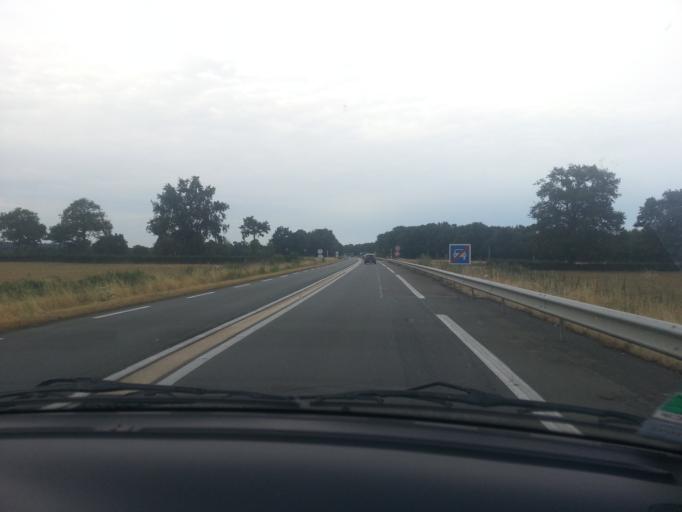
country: FR
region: Bourgogne
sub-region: Departement de Saone-et-Loire
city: Paray-le-Monial
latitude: 46.4805
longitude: 4.1456
